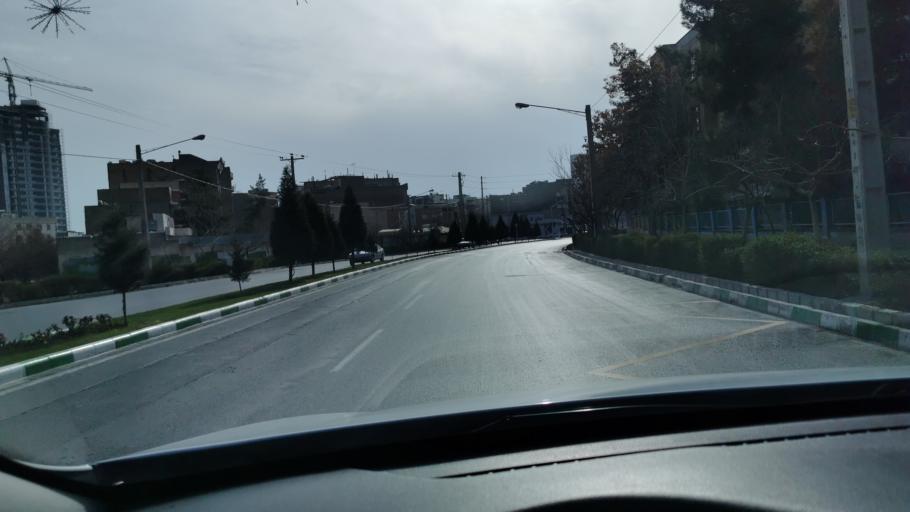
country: IR
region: Razavi Khorasan
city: Mashhad
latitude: 36.3135
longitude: 59.5136
